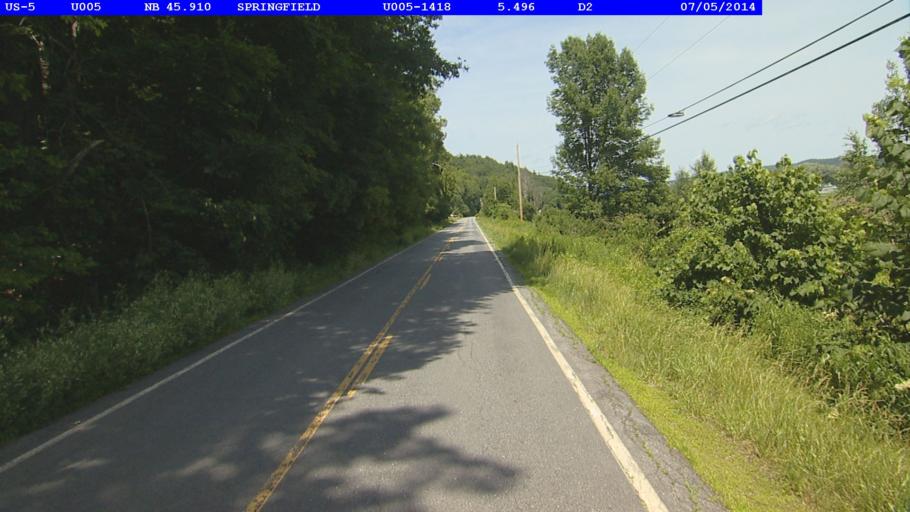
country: US
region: New Hampshire
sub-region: Sullivan County
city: Charlestown
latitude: 43.2928
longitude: -72.4117
